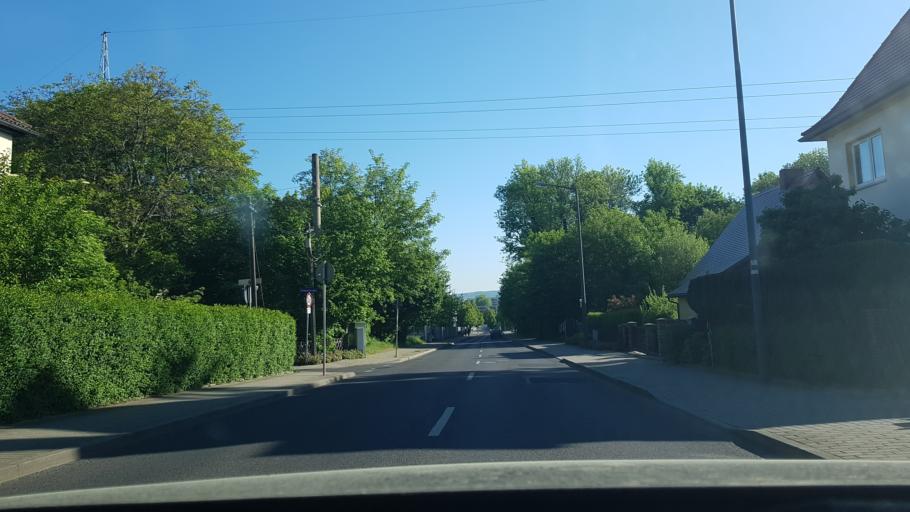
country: DE
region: Saxony
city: Kreischa
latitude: 50.9982
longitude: 13.7910
